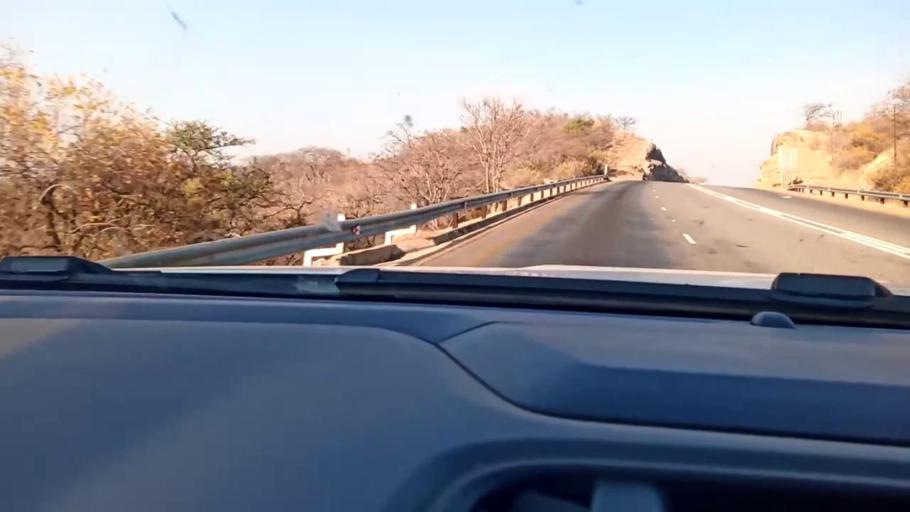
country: ZA
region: Limpopo
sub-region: Mopani District Municipality
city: Duiwelskloof
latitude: -23.6369
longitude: 30.1477
